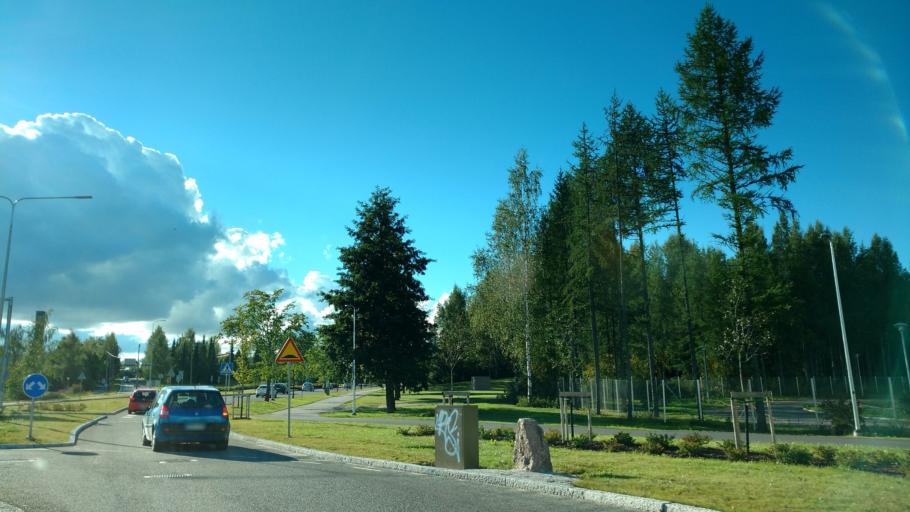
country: FI
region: Varsinais-Suomi
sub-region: Salo
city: Salo
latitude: 60.3920
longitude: 23.1135
